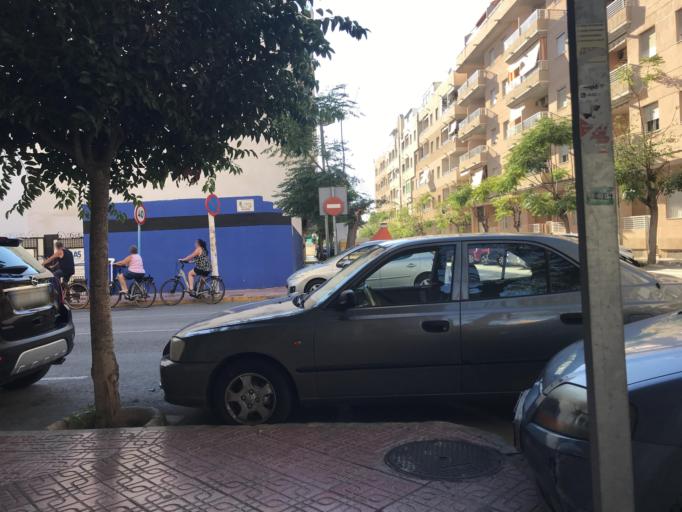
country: ES
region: Valencia
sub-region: Provincia de Alicante
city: Torrevieja
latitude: 37.9802
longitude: -0.6894
